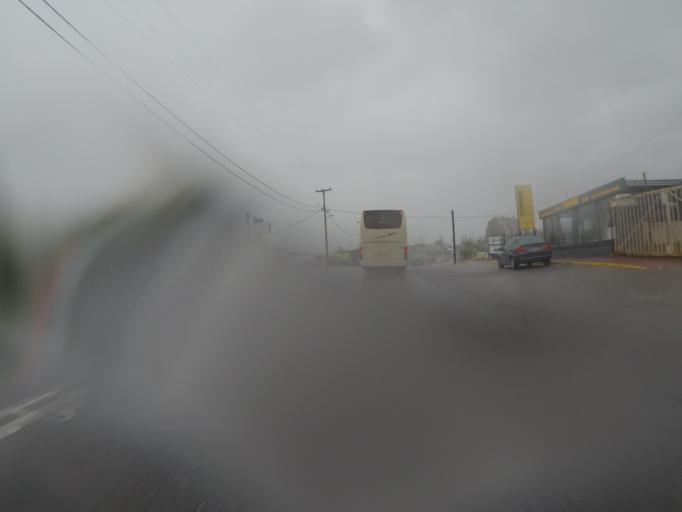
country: GR
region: Peloponnese
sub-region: Nomos Messinias
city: Kalamata
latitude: 37.0440
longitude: 22.0854
